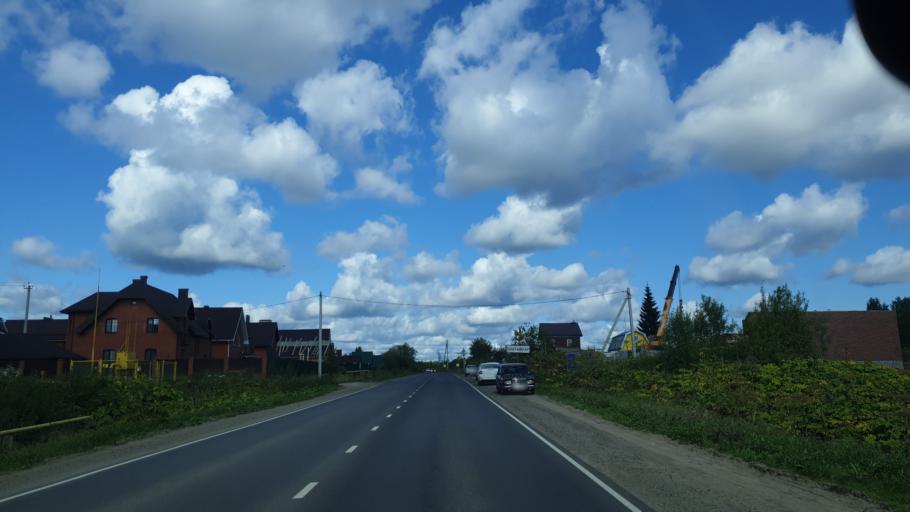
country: RU
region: Komi Republic
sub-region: Syktyvdinskiy Rayon
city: Syktyvkar
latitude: 61.6364
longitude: 50.8032
